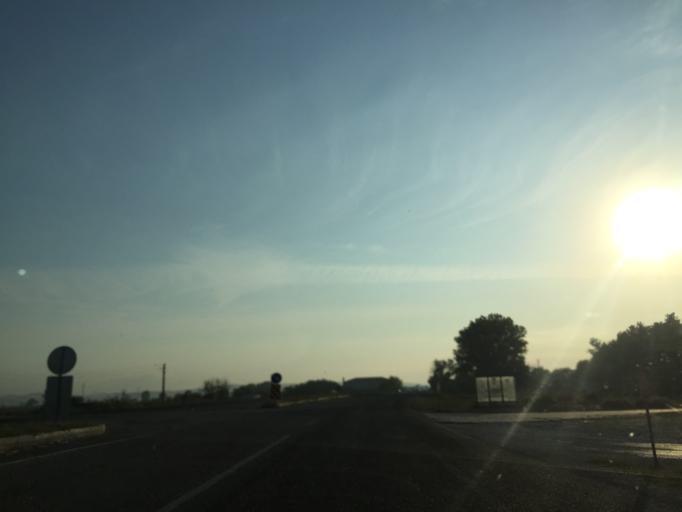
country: TR
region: Balikesir
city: Manyas
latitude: 40.0717
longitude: 28.0165
